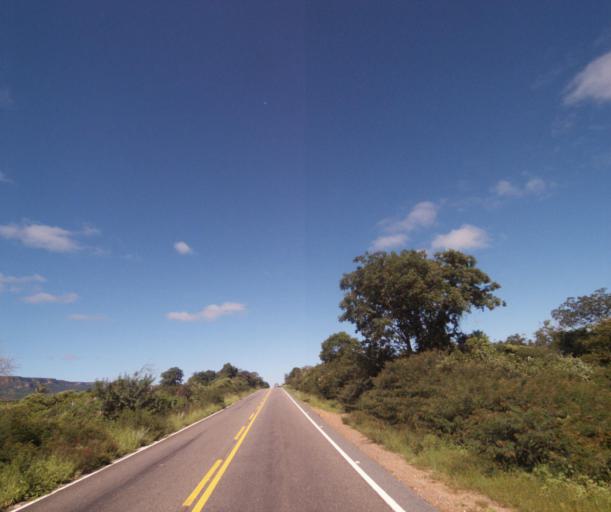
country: BR
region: Bahia
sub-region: Palmas De Monte Alto
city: Palmas de Monte Alto
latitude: -14.2431
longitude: -43.0835
